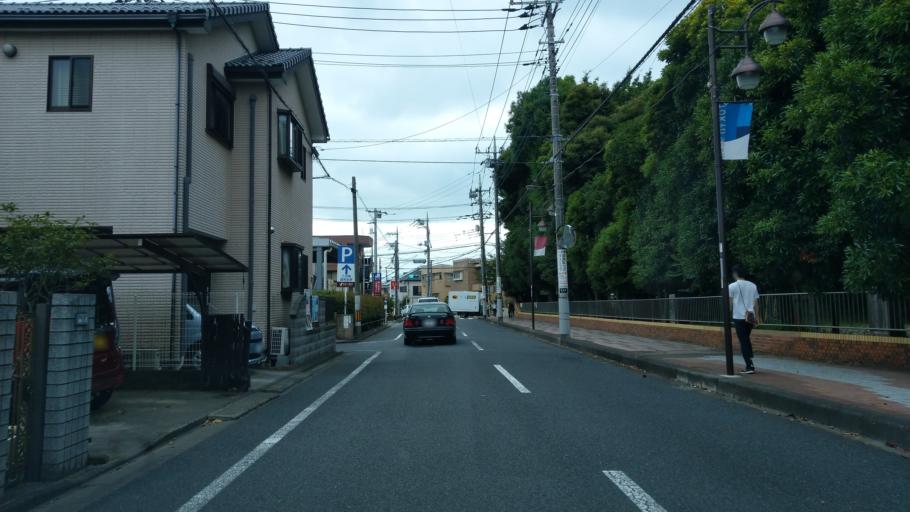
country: JP
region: Saitama
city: Saitama
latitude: 35.9290
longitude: 139.6264
